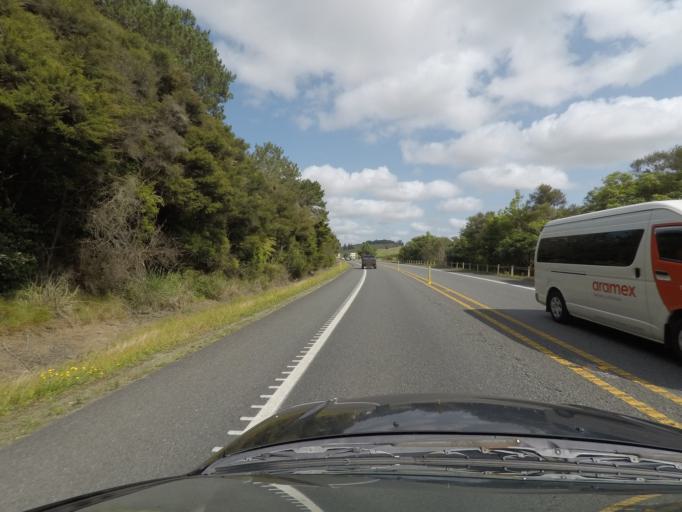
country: NZ
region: Northland
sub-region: Whangarei
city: Whangarei
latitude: -35.8218
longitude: 174.3051
